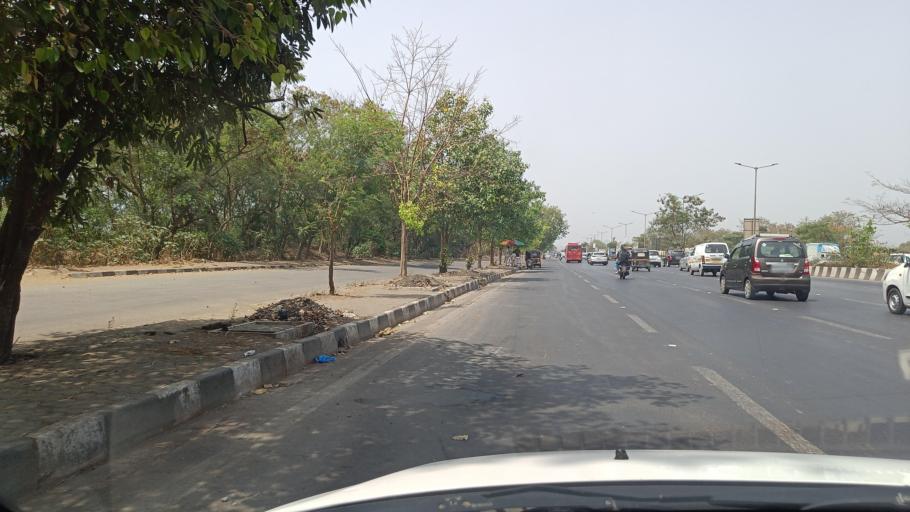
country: IN
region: Maharashtra
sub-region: Mumbai Suburban
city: Powai
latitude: 19.1330
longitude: 72.9432
